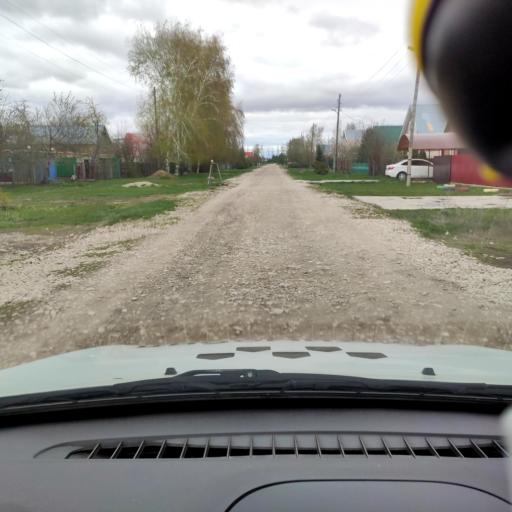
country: RU
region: Samara
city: Tol'yatti
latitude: 53.5805
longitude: 49.3298
